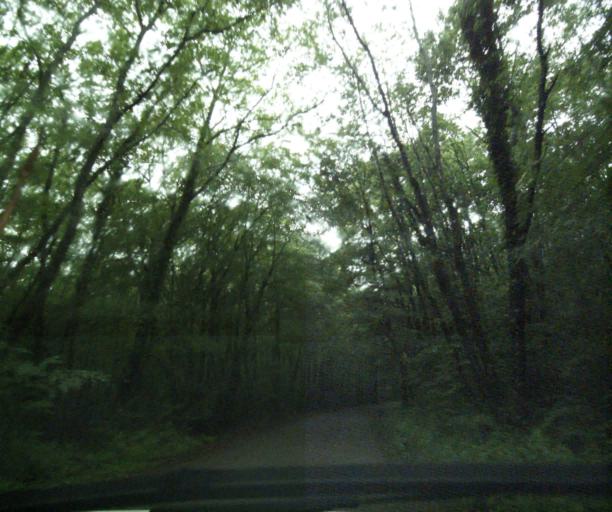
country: FR
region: Bourgogne
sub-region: Departement de Saone-et-Loire
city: Charolles
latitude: 46.3637
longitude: 4.1896
